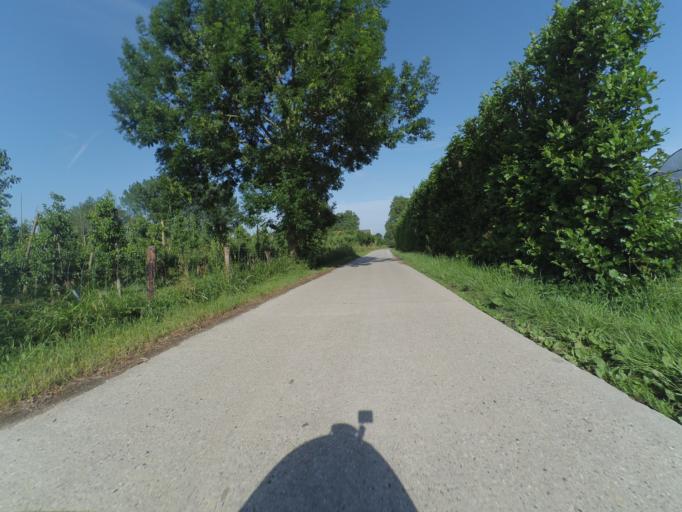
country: NL
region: Utrecht
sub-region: Gemeente Wijk bij Duurstede
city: Wijk bij Duurstede
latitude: 51.9658
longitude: 5.2933
